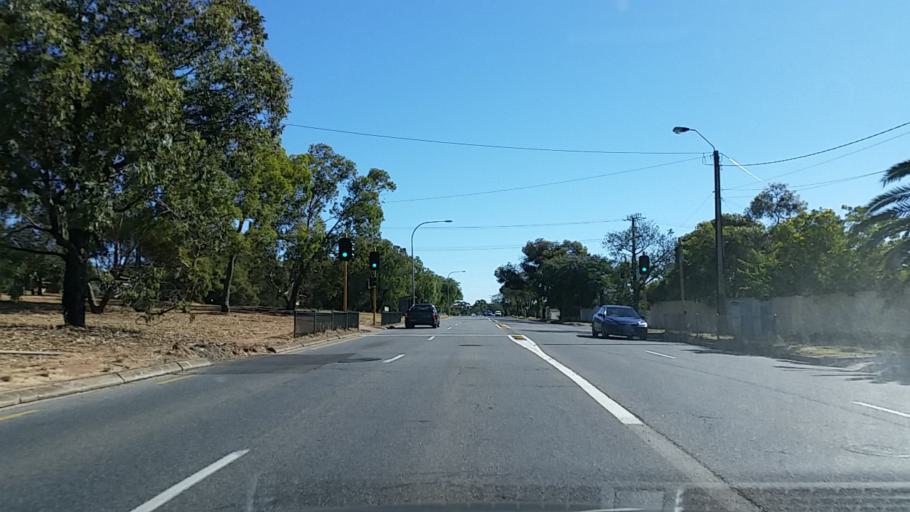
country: AU
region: South Australia
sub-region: Salisbury
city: Ingle Farm
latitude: -34.8320
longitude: 138.6287
